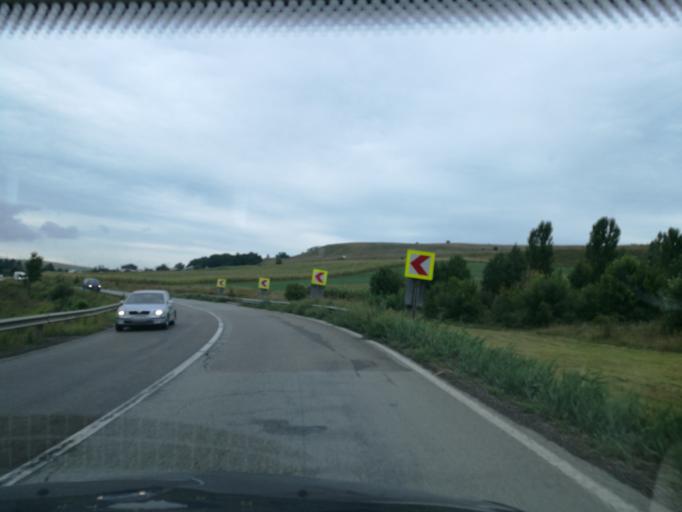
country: RO
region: Suceava
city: Bunesti-Regat
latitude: 47.5144
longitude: 26.2869
